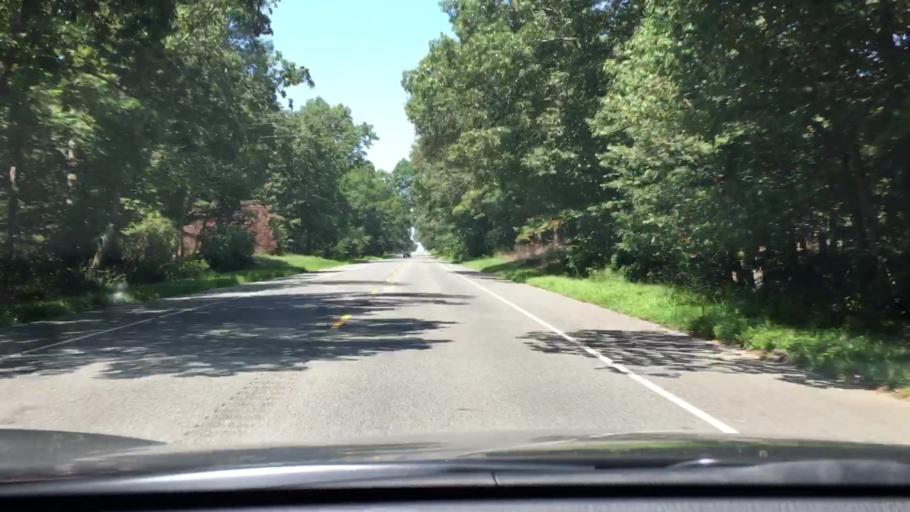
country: US
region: New Jersey
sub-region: Cumberland County
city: Laurel Lake
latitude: 39.3497
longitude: -75.0520
